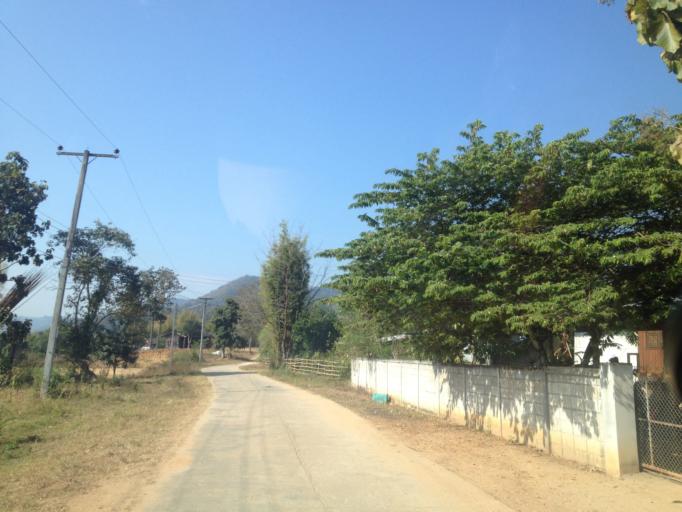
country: TH
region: Mae Hong Son
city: Ban Huai I Huak
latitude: 18.1069
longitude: 98.2151
